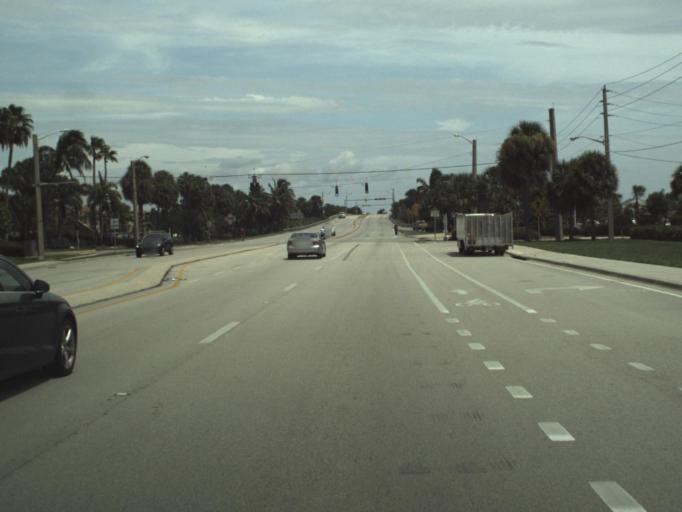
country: US
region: Florida
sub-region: Palm Beach County
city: Jupiter
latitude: 26.9433
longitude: -80.0844
